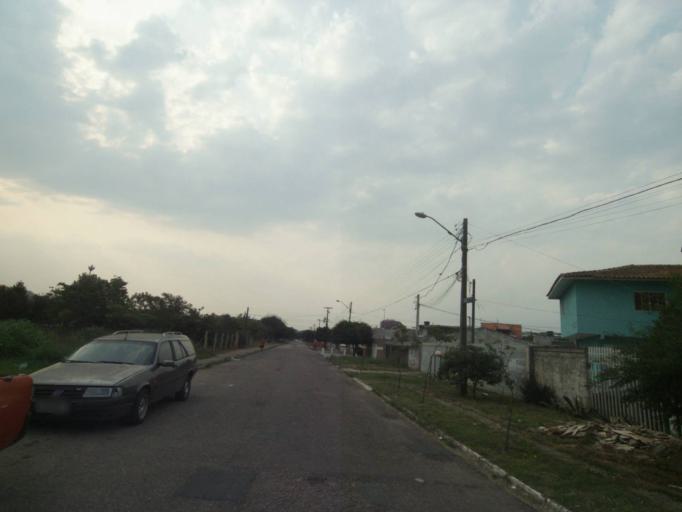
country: BR
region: Parana
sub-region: Sao Jose Dos Pinhais
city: Sao Jose dos Pinhais
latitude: -25.5357
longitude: -49.2509
